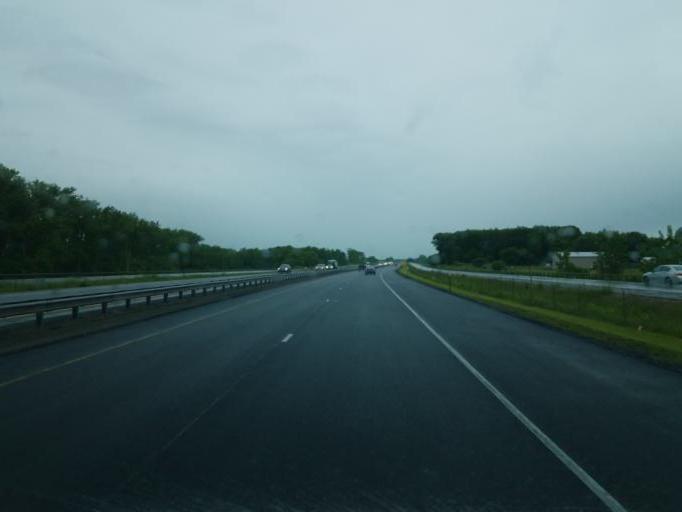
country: US
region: New York
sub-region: Oneida County
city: Yorkville
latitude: 43.1280
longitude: -75.2525
